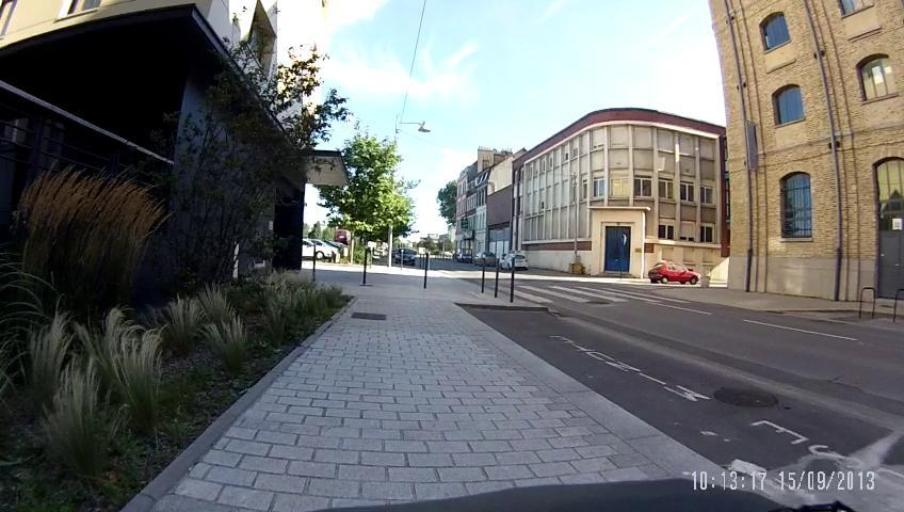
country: FR
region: Nord-Pas-de-Calais
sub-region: Departement du Nord
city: Dunkerque
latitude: 51.0386
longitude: 2.3708
